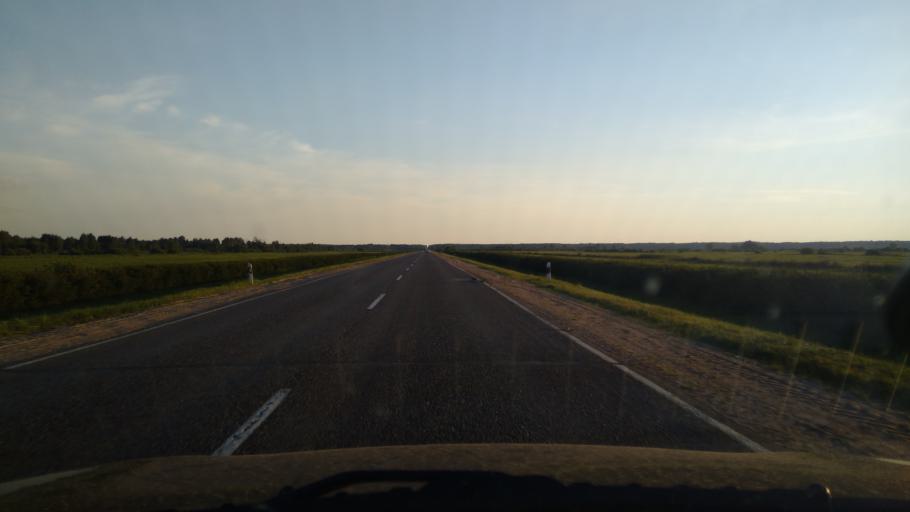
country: BY
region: Brest
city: Nyakhachava
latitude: 52.6303
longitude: 25.1787
